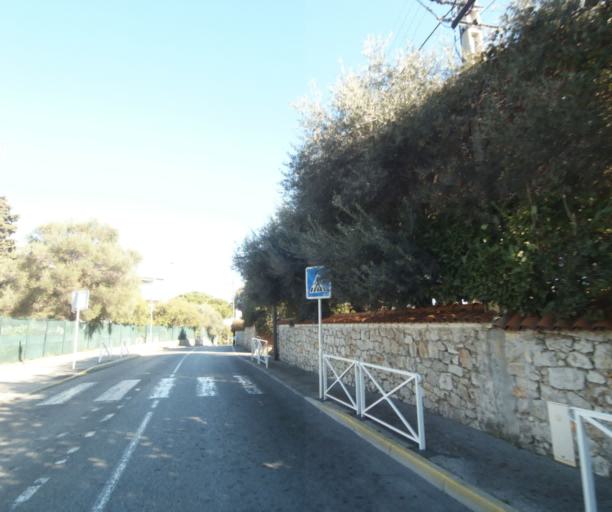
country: FR
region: Provence-Alpes-Cote d'Azur
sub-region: Departement des Alpes-Maritimes
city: Antibes
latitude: 43.5731
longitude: 7.1192
